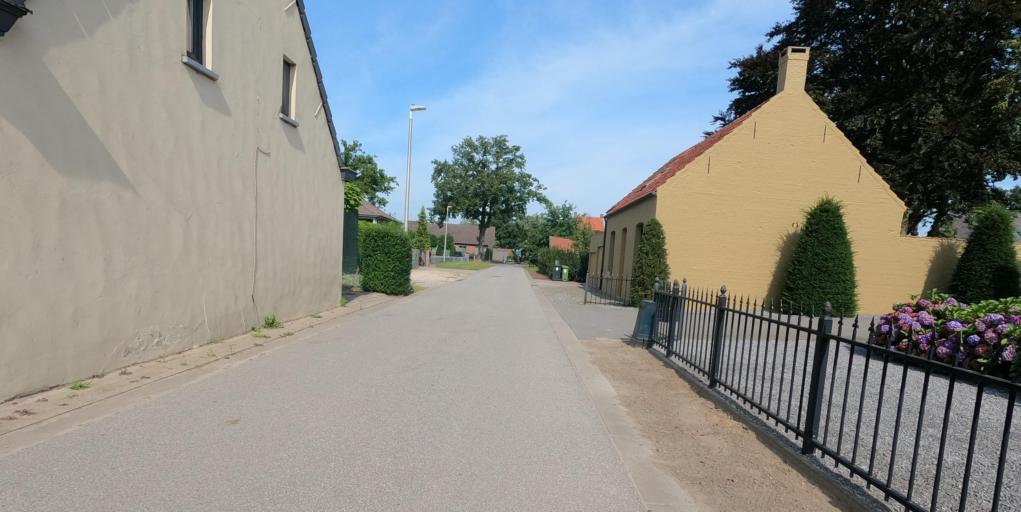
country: BE
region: Flanders
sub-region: Provincie Antwerpen
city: Essen
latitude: 51.4470
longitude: 4.4190
